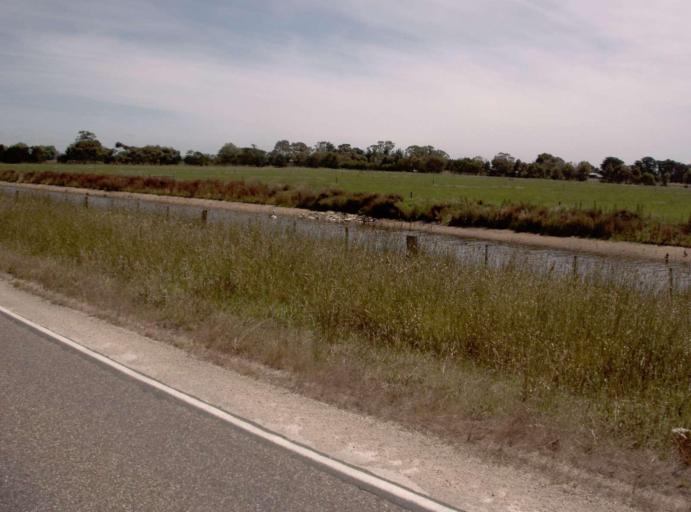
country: AU
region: Victoria
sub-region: Wellington
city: Heyfield
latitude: -38.0501
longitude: 146.8751
